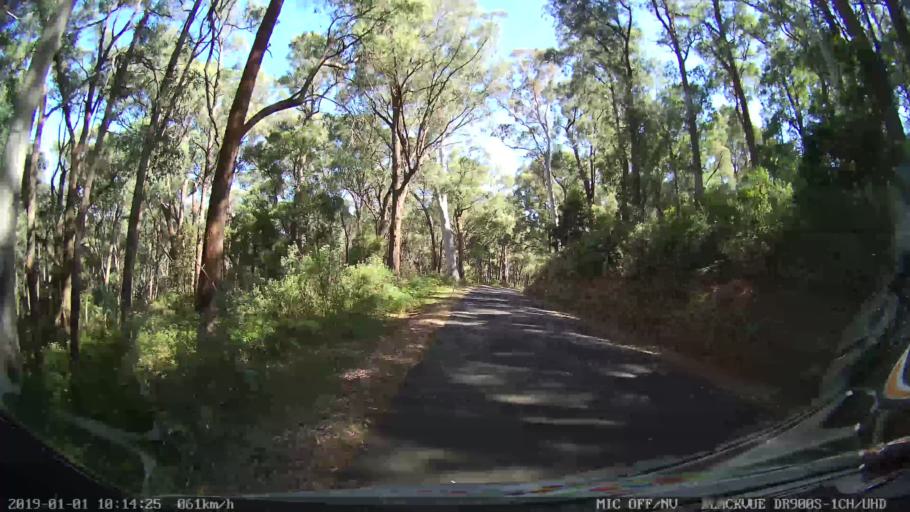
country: AU
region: New South Wales
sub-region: Snowy River
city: Jindabyne
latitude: -36.1125
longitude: 148.1607
